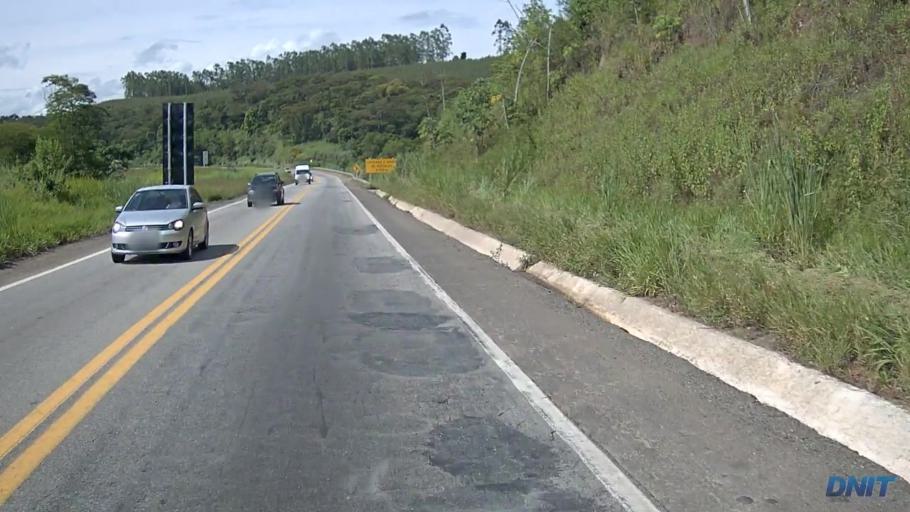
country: BR
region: Minas Gerais
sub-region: Ipaba
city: Ipaba
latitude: -19.4052
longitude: -42.4850
